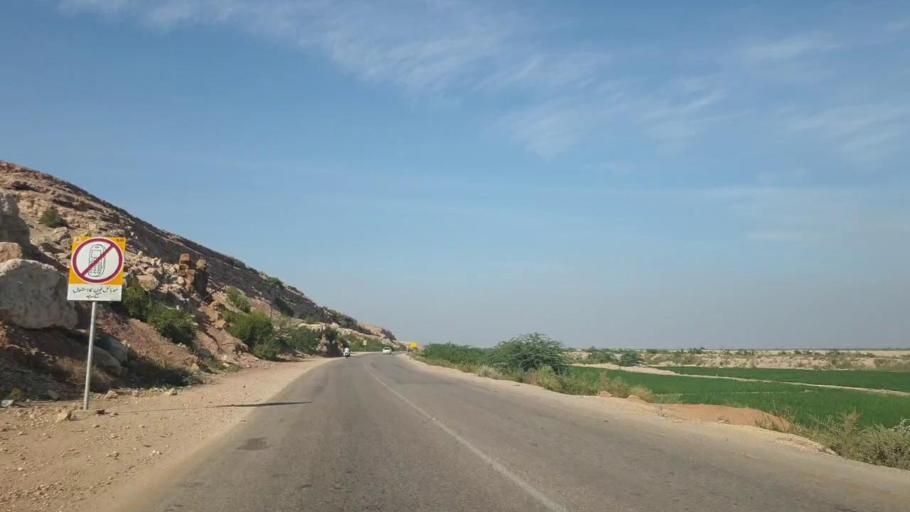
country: PK
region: Sindh
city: Sehwan
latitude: 26.3647
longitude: 67.8738
